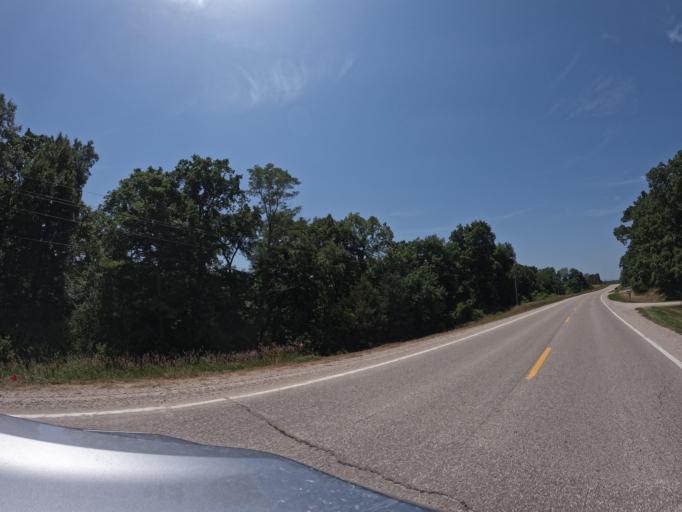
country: US
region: Iowa
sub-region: Henry County
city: Mount Pleasant
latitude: 40.9371
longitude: -91.5987
